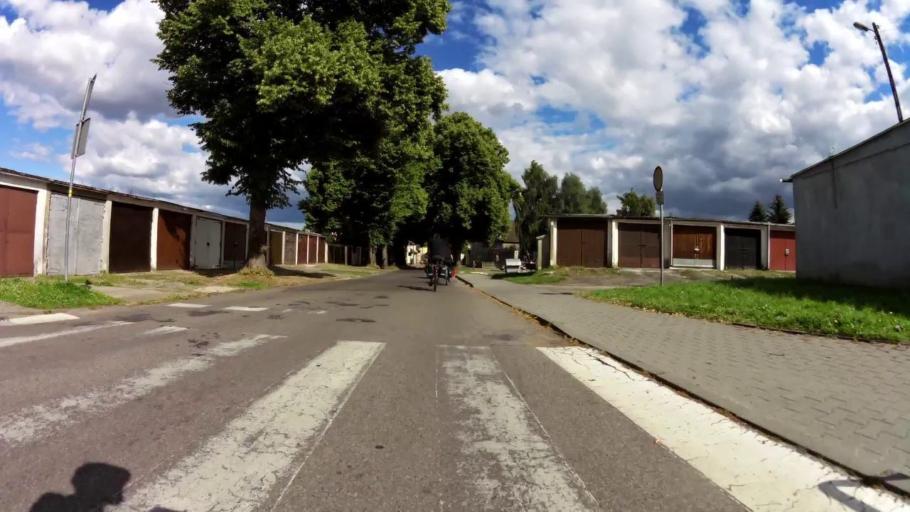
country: PL
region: West Pomeranian Voivodeship
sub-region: Powiat lobeski
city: Lobez
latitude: 53.6383
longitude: 15.6148
